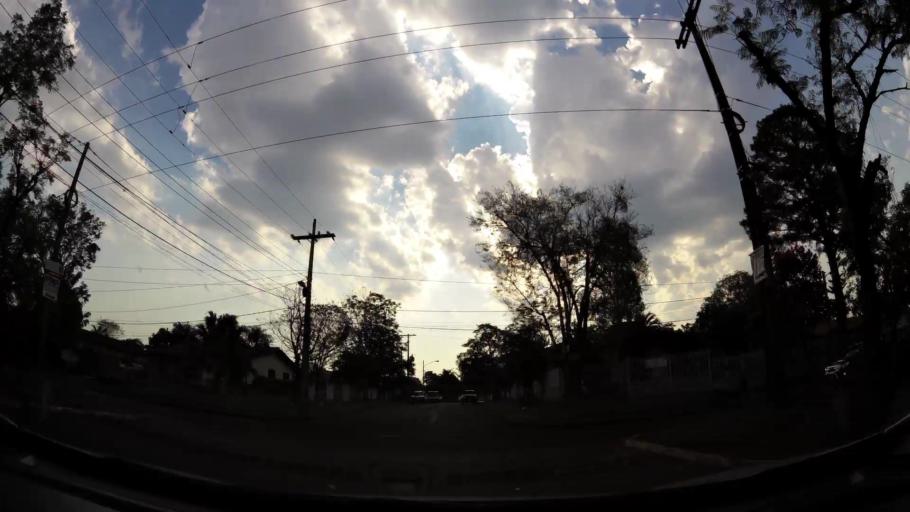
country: PY
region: Alto Parana
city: Presidente Franco
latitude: -25.5204
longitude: -54.6338
